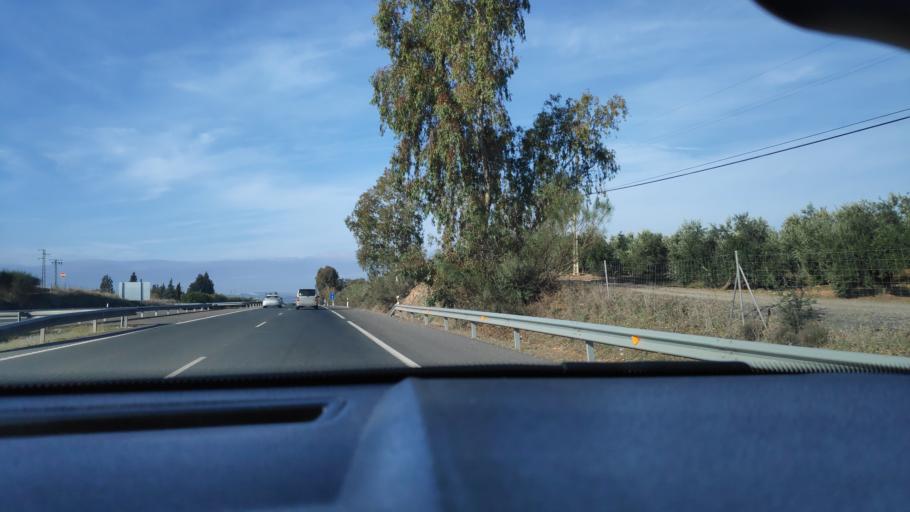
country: ES
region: Andalusia
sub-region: Provincia de Jaen
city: Linares
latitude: 38.0949
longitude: -3.6906
